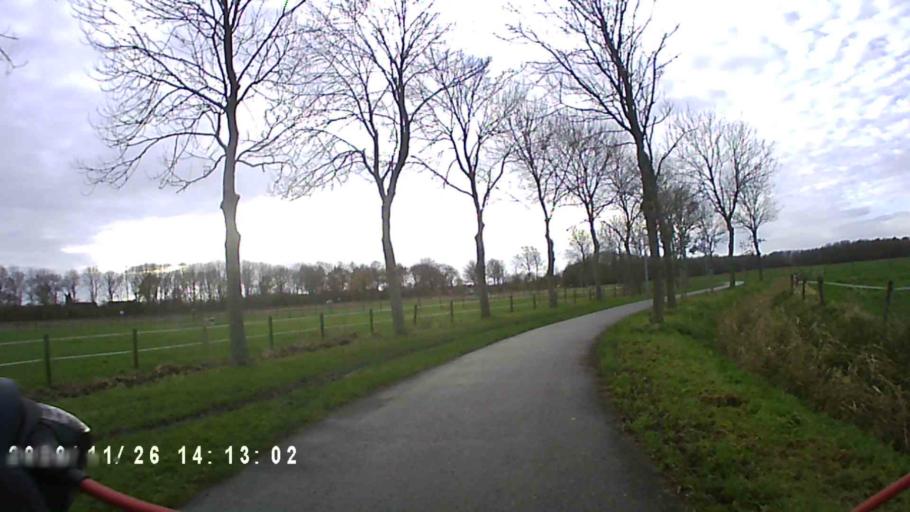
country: NL
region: Groningen
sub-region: Gemeente Delfzijl
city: Delfzijl
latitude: 53.3318
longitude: 6.8949
